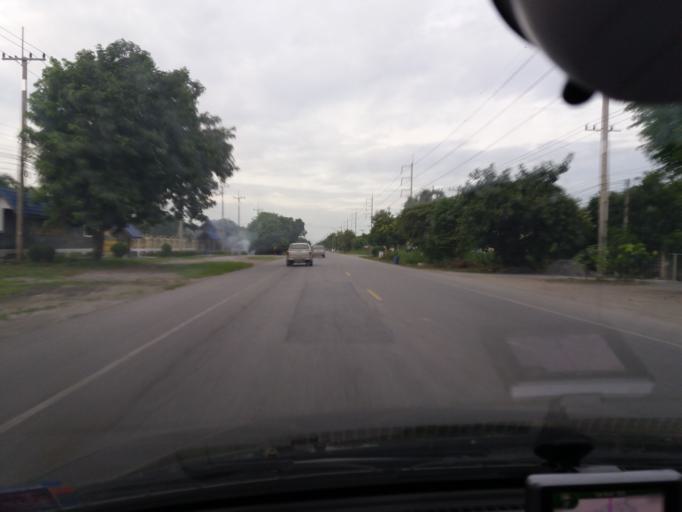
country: TH
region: Suphan Buri
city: U Thong
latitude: 14.4995
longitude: 99.9193
